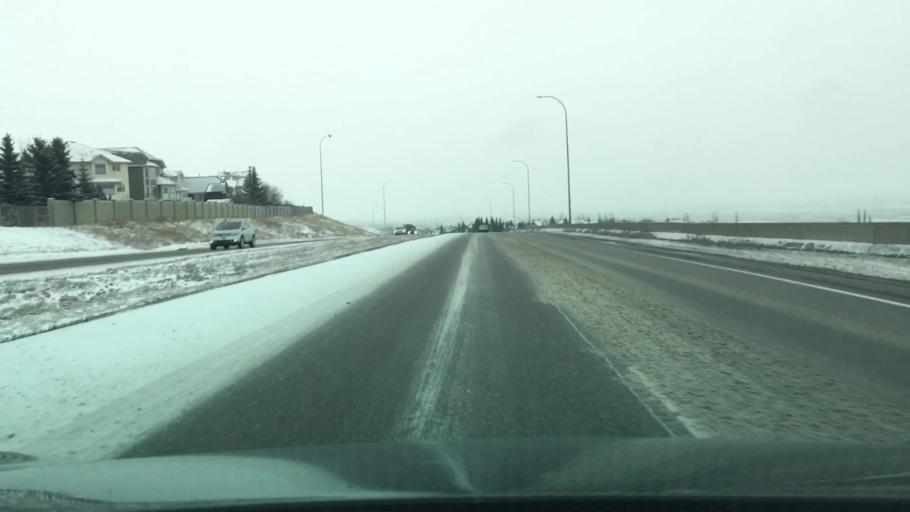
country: CA
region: Alberta
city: Calgary
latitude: 51.1301
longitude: -114.1280
